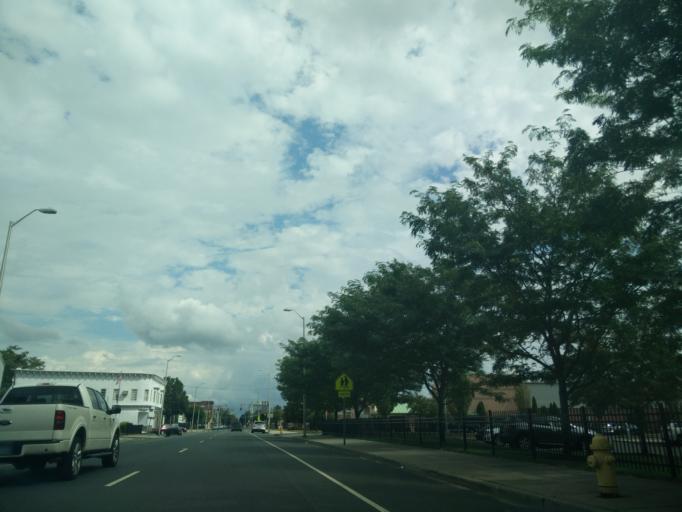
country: US
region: Connecticut
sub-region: Fairfield County
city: Bridgeport
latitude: 41.1700
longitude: -73.2107
